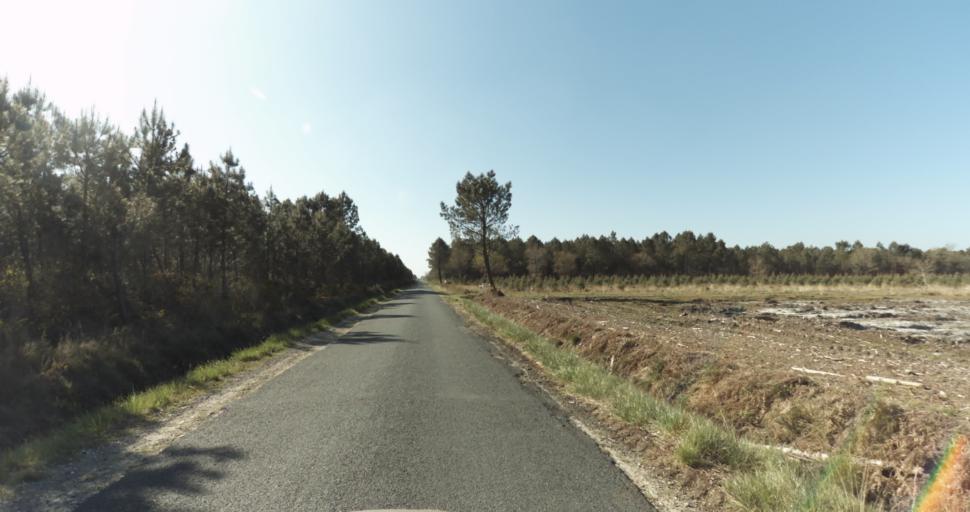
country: FR
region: Aquitaine
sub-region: Departement de la Gironde
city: Marcheprime
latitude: 44.7885
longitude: -0.8634
